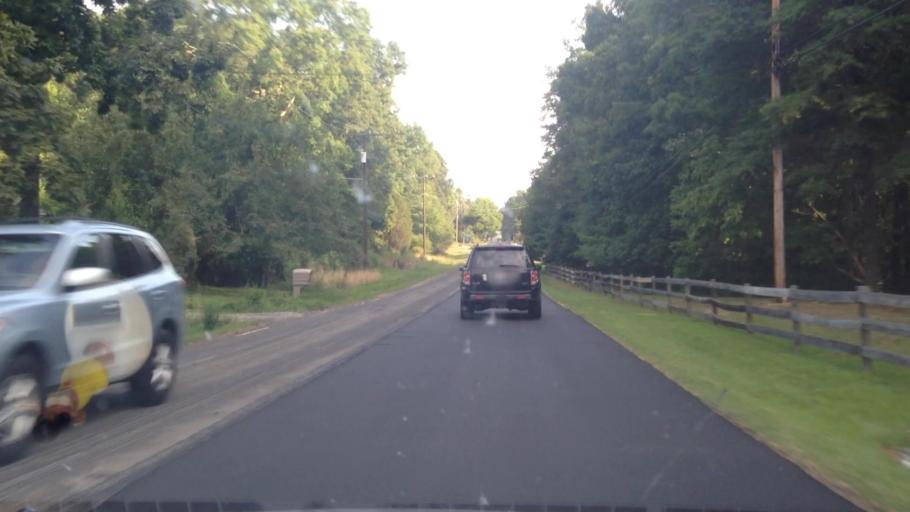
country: US
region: North Carolina
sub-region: Davidson County
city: Wallburg
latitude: 36.0178
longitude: -80.0601
